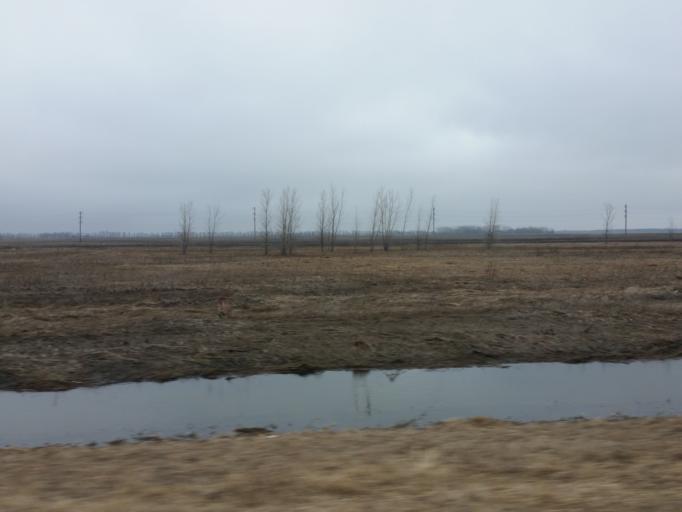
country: US
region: North Dakota
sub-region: Walsh County
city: Grafton
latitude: 48.3532
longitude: -97.1839
